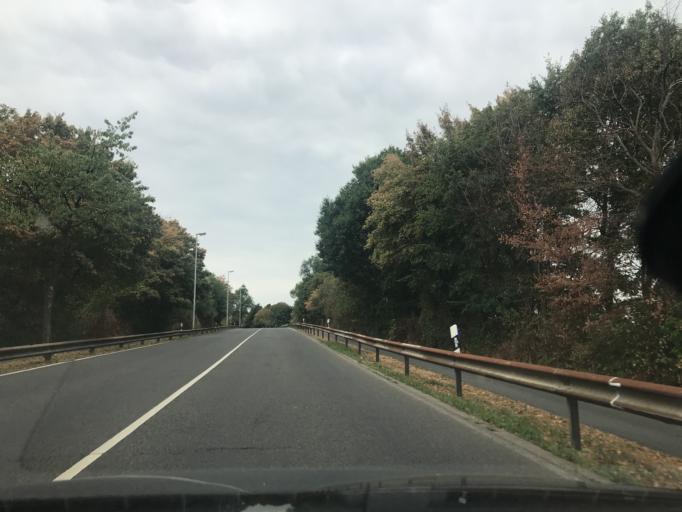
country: DE
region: North Rhine-Westphalia
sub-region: Regierungsbezirk Dusseldorf
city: Krefeld
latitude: 51.3757
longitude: 6.6255
